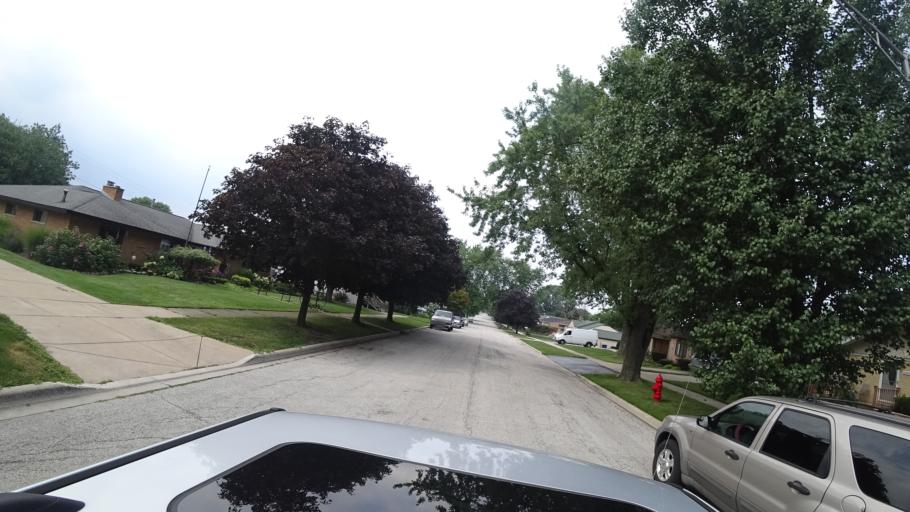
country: US
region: Illinois
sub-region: Cook County
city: Chicago Ridge
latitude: 41.6982
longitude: -87.7767
